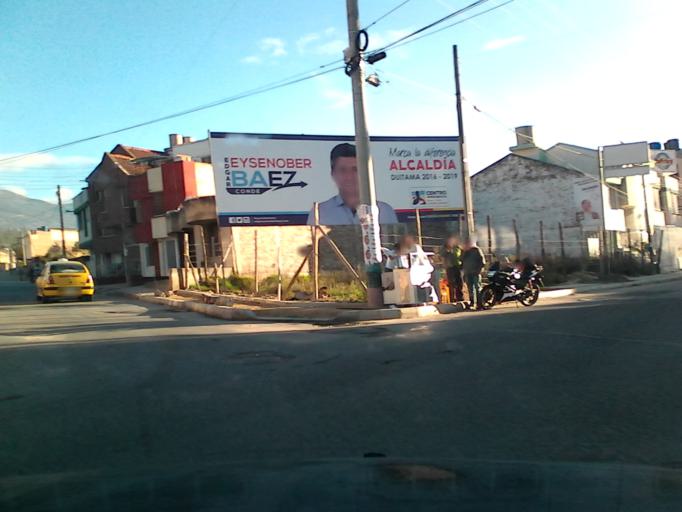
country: CO
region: Boyaca
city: Duitama
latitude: 5.8337
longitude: -73.0298
